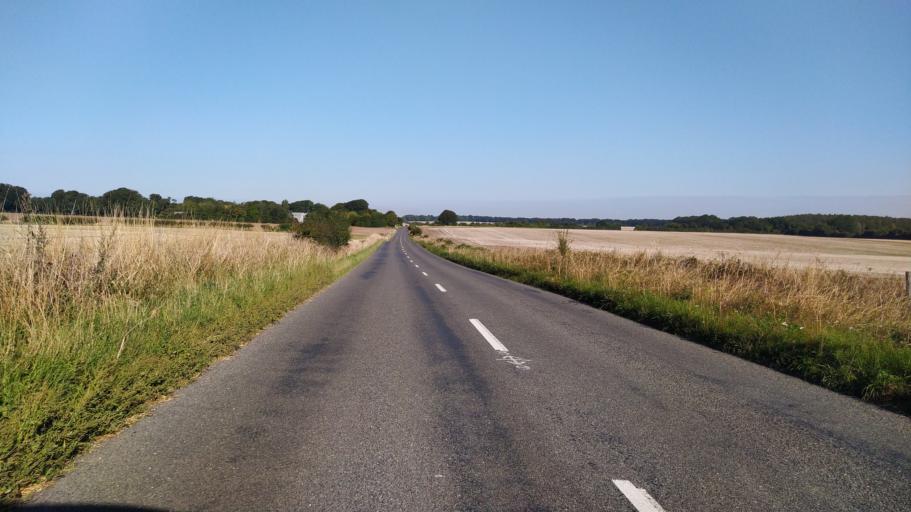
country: GB
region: England
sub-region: Hampshire
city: Abbotts Ann
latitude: 51.1431
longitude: -1.5331
